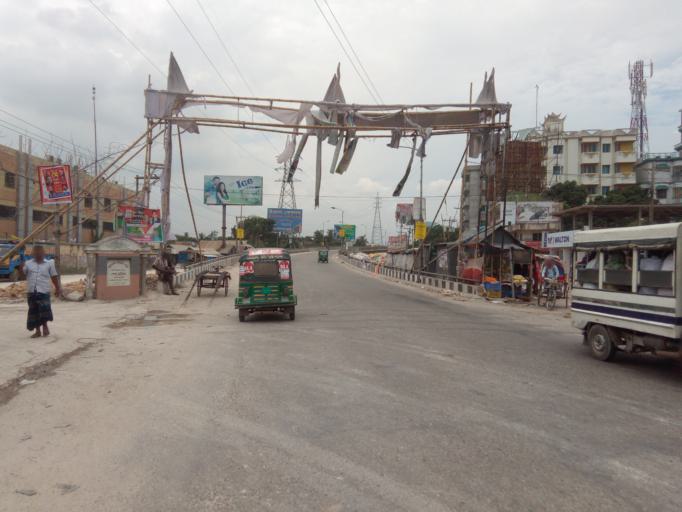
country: BD
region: Dhaka
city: Paltan
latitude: 23.7225
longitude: 90.5069
